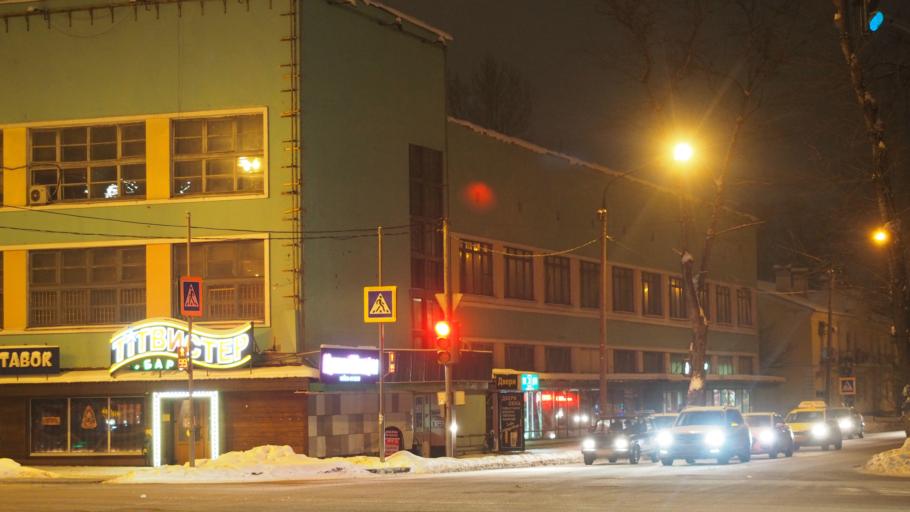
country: RU
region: Moskovskaya
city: Yubileyny
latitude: 55.9136
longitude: 37.8563
